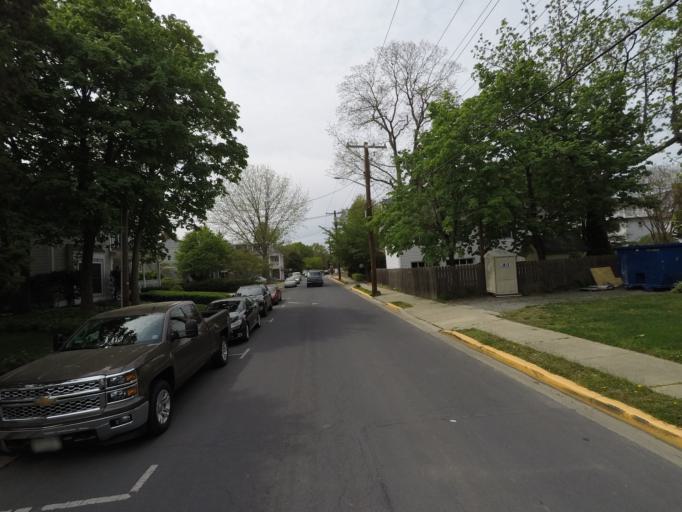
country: US
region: Delaware
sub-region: Sussex County
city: Lewes
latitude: 38.7757
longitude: -75.1422
